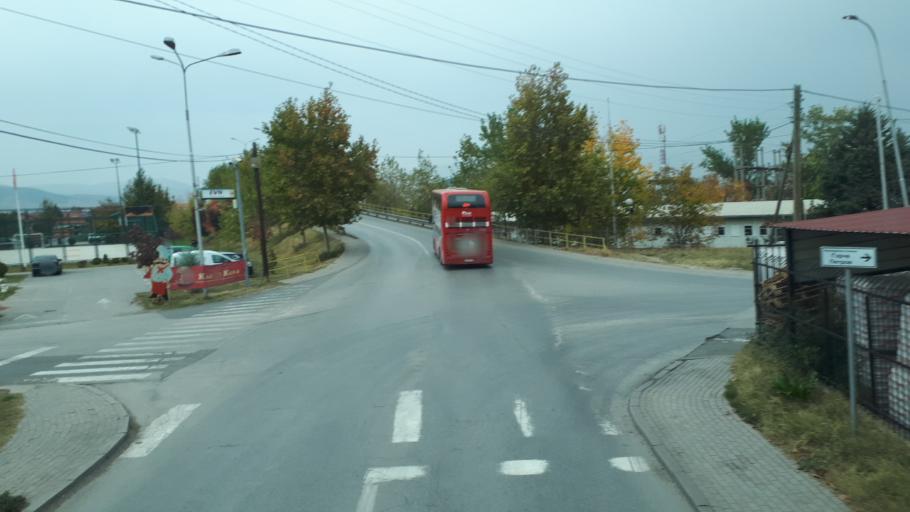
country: MK
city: Krushopek
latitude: 42.0114
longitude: 21.3601
